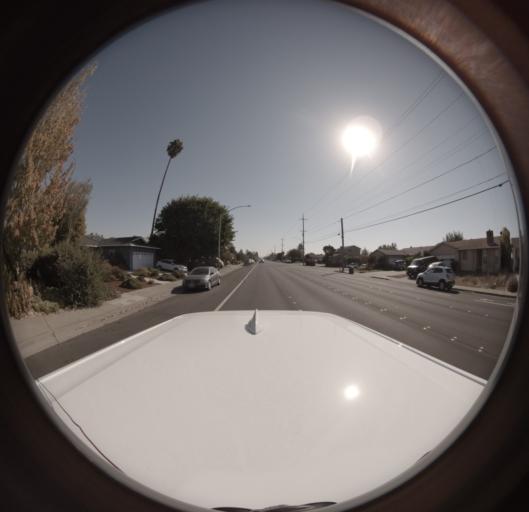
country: US
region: California
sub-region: Sonoma County
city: Petaluma
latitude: 38.2546
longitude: -122.6155
